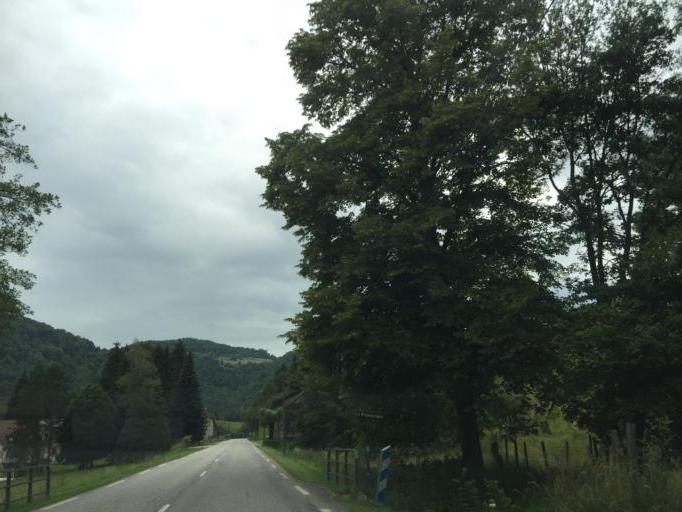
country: FR
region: Rhone-Alpes
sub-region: Departement de la Savoie
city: Les Echelles
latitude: 45.4635
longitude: 5.7370
